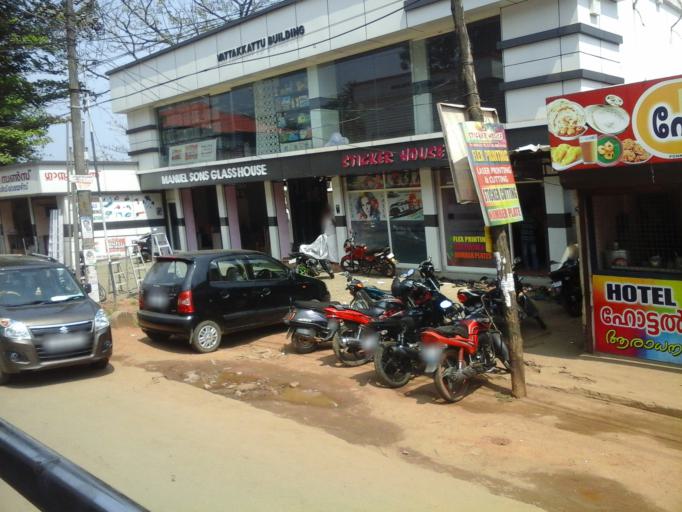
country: IN
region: Kerala
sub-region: Kottayam
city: Erattupetta
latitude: 9.5666
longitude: 76.7541
